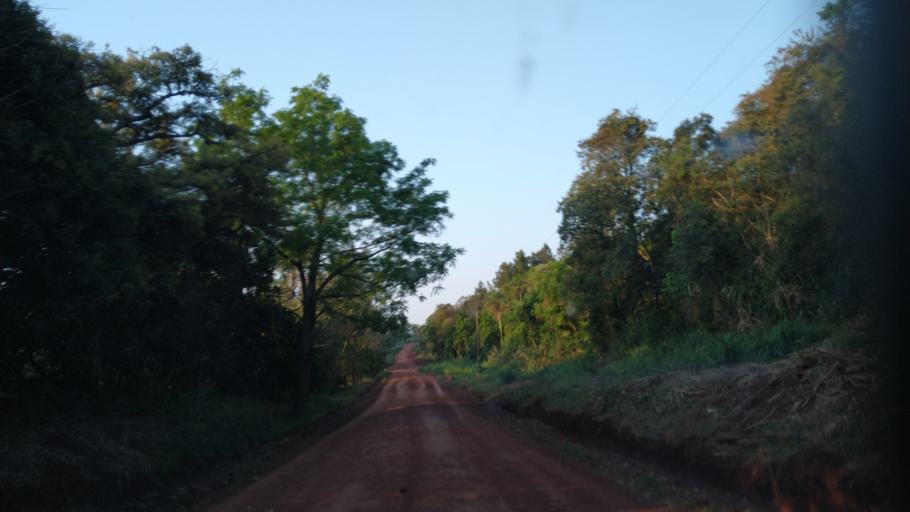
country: AR
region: Misiones
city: Jardin America
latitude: -27.0677
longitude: -55.2664
